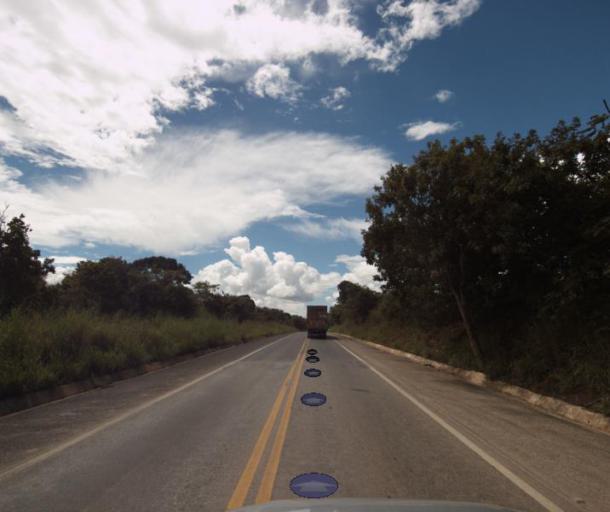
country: BR
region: Goias
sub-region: Uruacu
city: Uruacu
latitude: -14.1295
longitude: -49.1109
